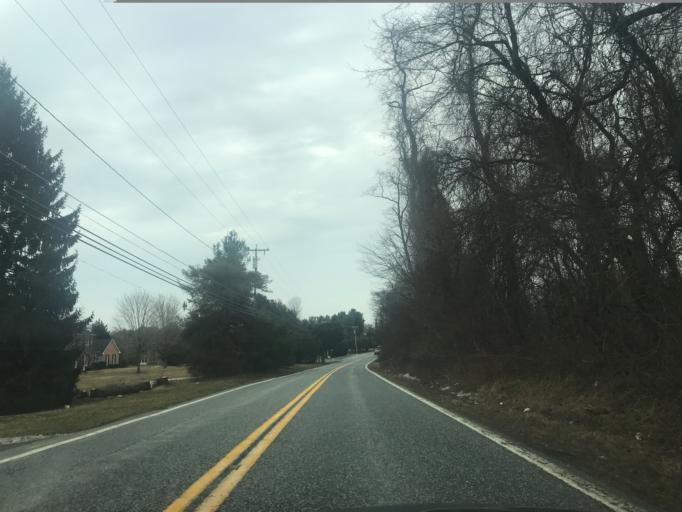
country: US
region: Maryland
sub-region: Harford County
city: Jarrettsville
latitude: 39.5811
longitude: -76.5016
